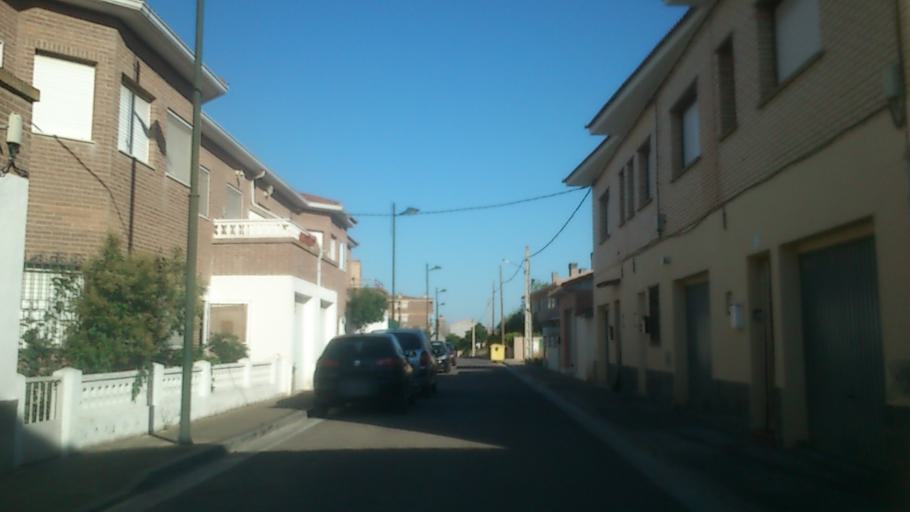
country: ES
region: Aragon
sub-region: Provincia de Zaragoza
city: San Mateo de Gallego
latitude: 41.8297
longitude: -0.7632
